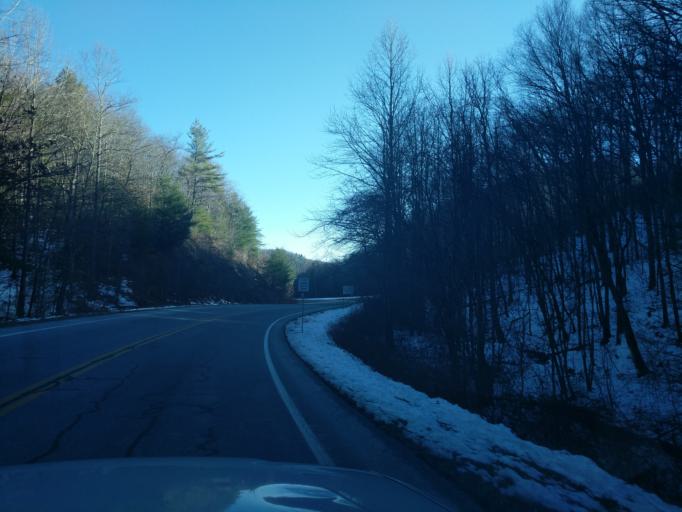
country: US
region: Georgia
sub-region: Towns County
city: Hiawassee
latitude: 34.9110
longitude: -83.6178
